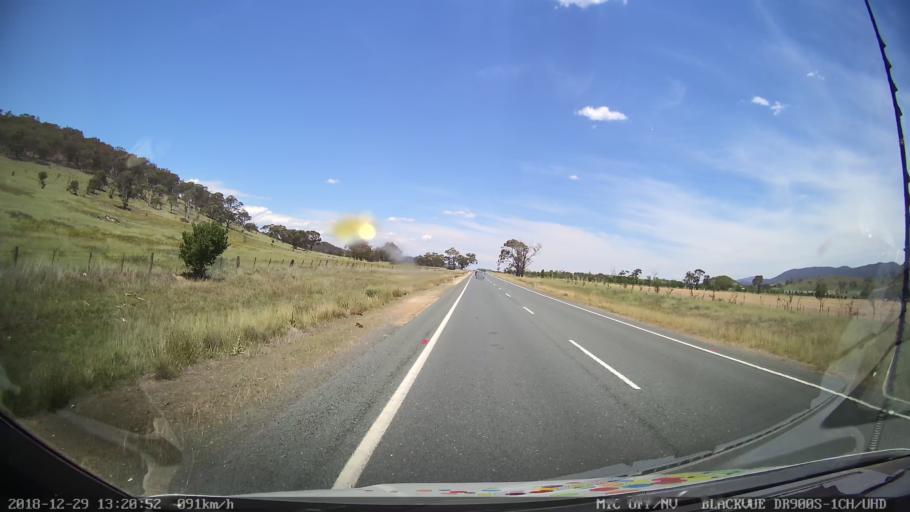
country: AU
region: Australian Capital Territory
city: Macarthur
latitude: -35.7847
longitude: 149.1625
